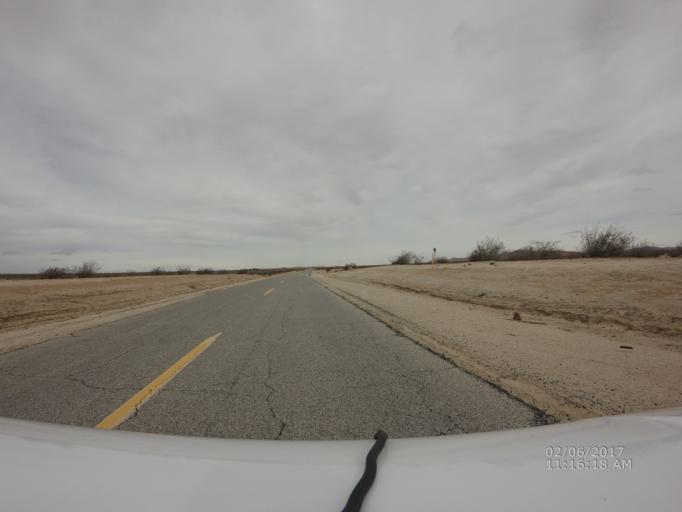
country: US
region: California
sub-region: Los Angeles County
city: Lake Los Angeles
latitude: 34.6748
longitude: -117.7025
